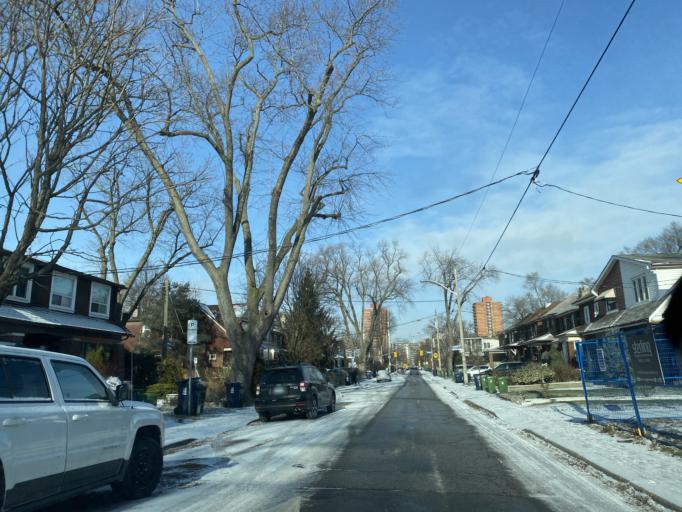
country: CA
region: Ontario
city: Toronto
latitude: 43.6836
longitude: -79.3515
